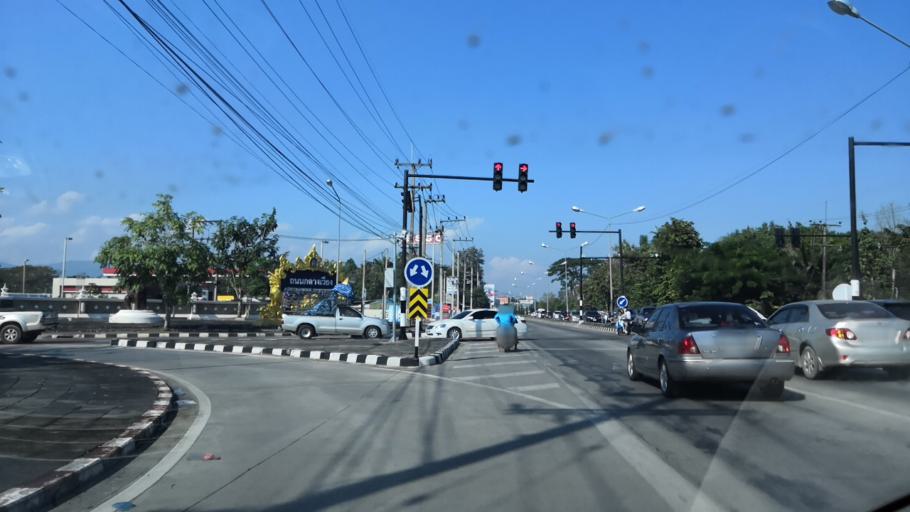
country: TH
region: Chiang Rai
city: Chiang Rai
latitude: 19.9368
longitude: 99.8451
